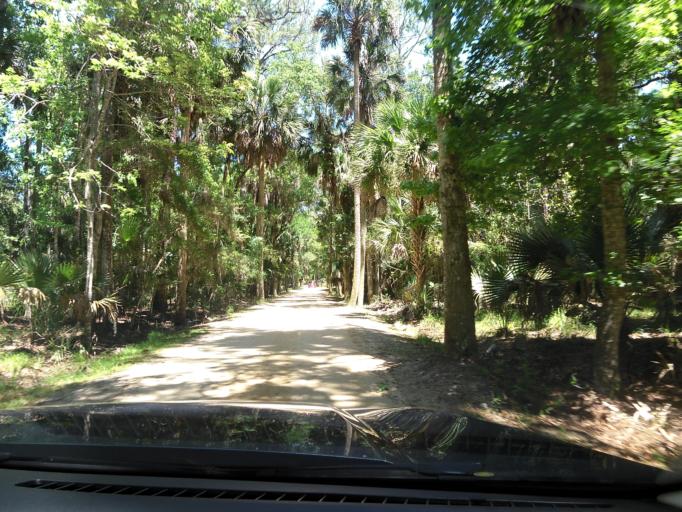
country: US
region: Florida
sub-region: Flagler County
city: Flagler Beach
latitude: 29.4335
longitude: -81.1415
